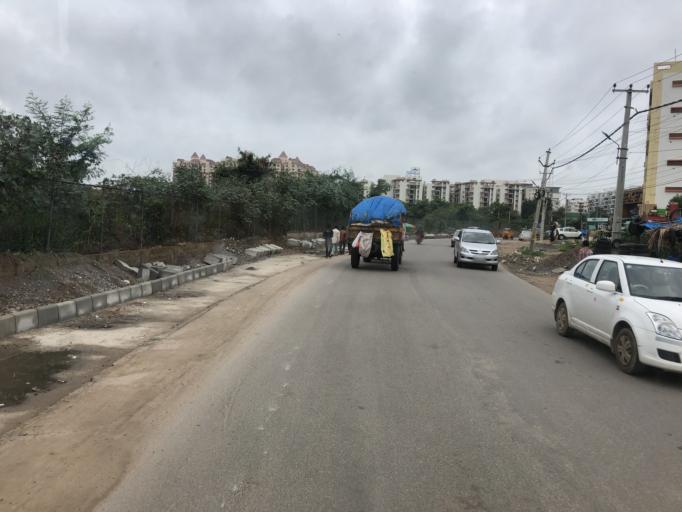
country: IN
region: Telangana
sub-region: Rangareddi
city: Kukatpalli
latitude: 17.4647
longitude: 78.3745
